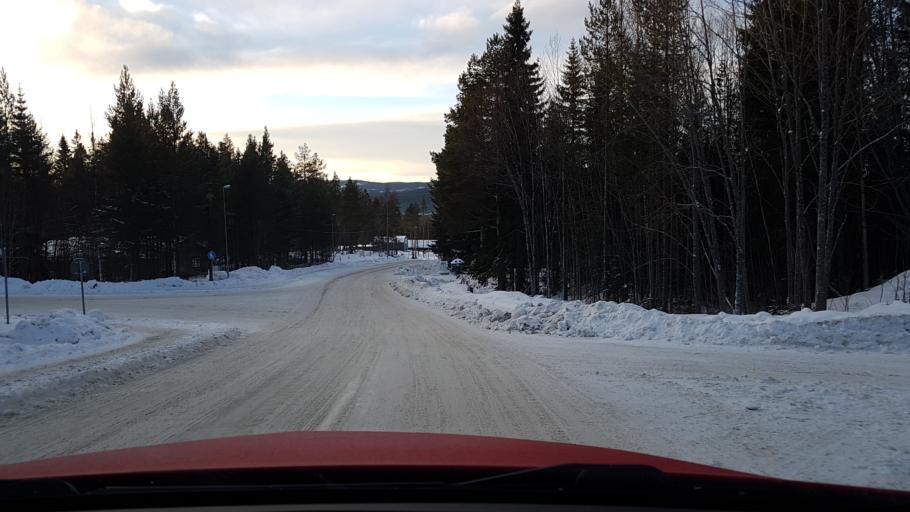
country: SE
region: Jaemtland
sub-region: Harjedalens Kommun
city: Sveg
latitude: 62.4175
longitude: 13.9459
